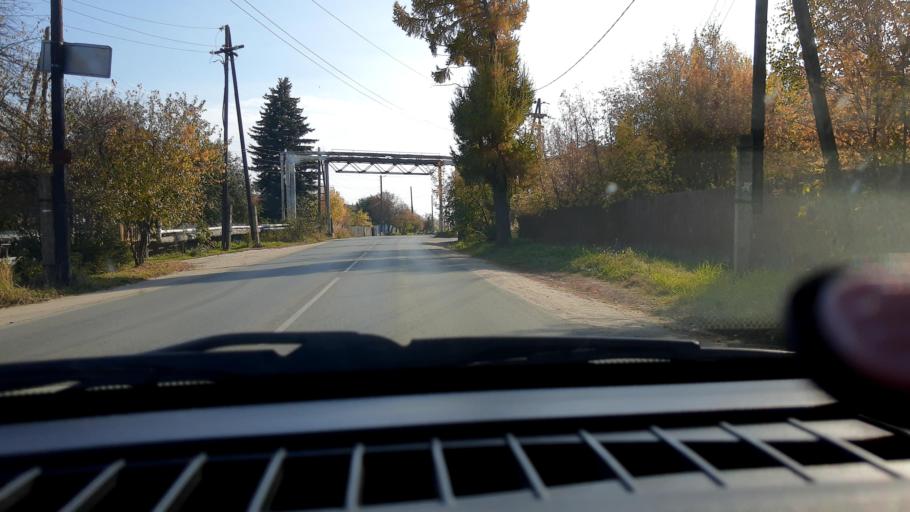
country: RU
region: Nizjnij Novgorod
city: Gorodets
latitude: 56.6457
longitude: 43.4886
